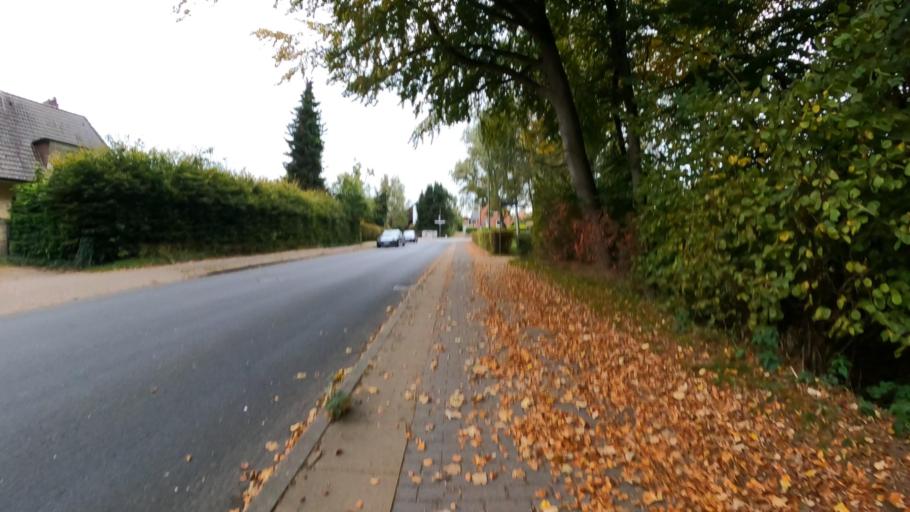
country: DE
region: Schleswig-Holstein
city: Ahrensburg
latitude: 53.6587
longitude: 10.2428
